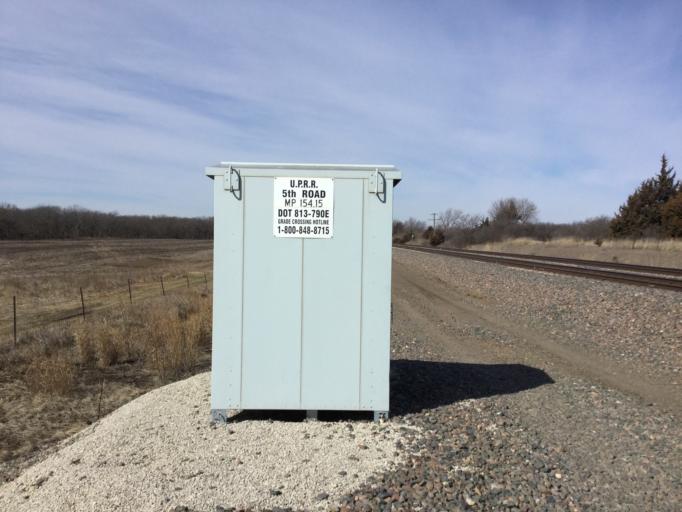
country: US
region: Kansas
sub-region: Marshall County
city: Marysville
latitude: 39.8927
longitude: -96.7305
